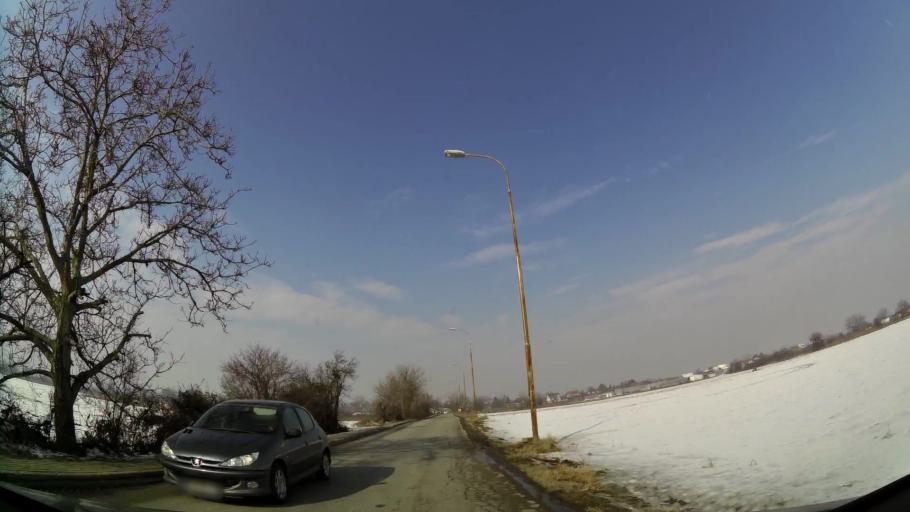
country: MK
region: Suto Orizari
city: Suto Orizare
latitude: 42.0213
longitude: 21.3869
